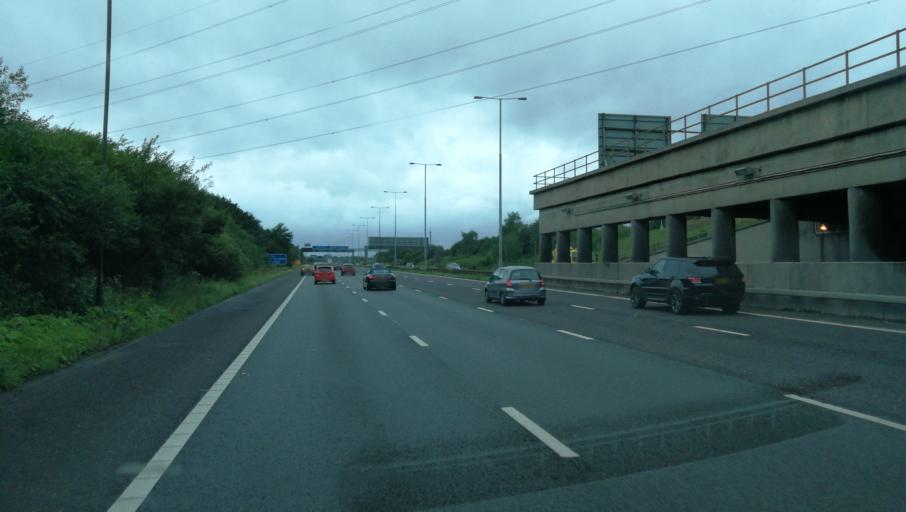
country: GB
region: England
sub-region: Borough of Bolton
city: Kearsley
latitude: 53.5289
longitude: -2.3686
